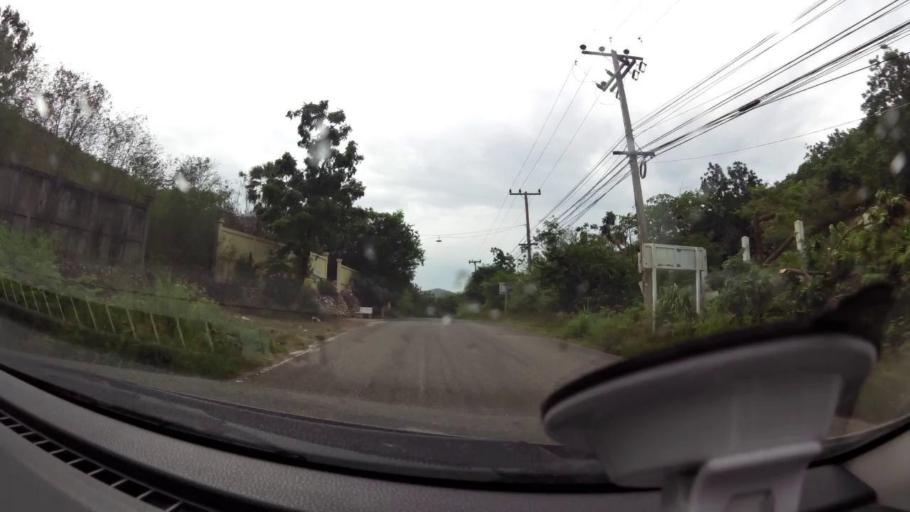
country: TH
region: Prachuap Khiri Khan
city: Pran Buri
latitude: 12.4388
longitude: 99.9712
